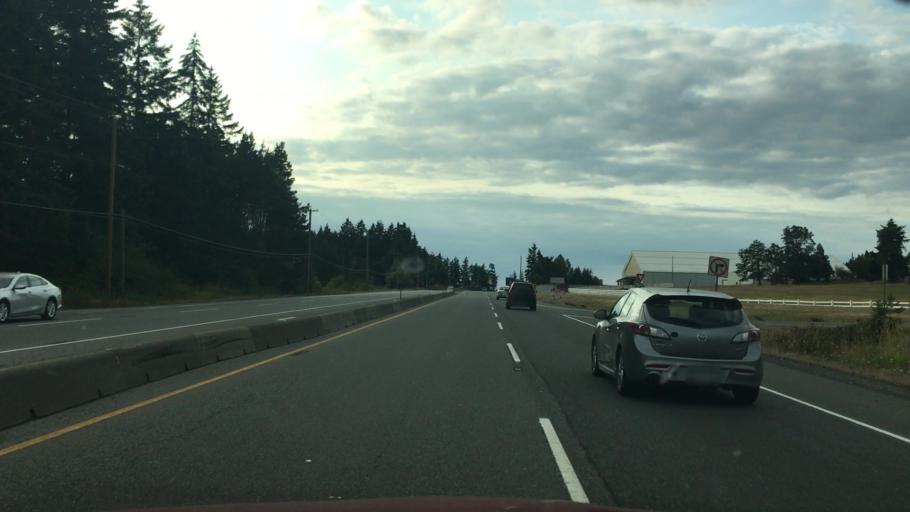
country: CA
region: British Columbia
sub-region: Regional District of Nanaimo
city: Parksville
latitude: 49.2786
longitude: -124.2434
